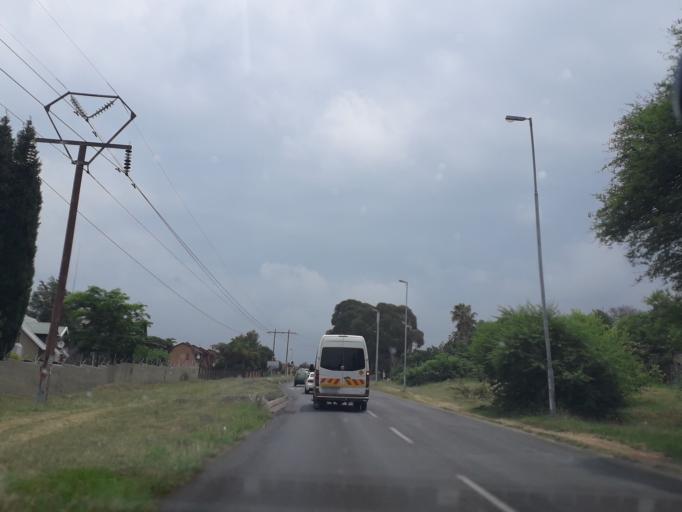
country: ZA
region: Gauteng
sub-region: City of Johannesburg Metropolitan Municipality
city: Roodepoort
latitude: -26.0784
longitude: 27.9530
